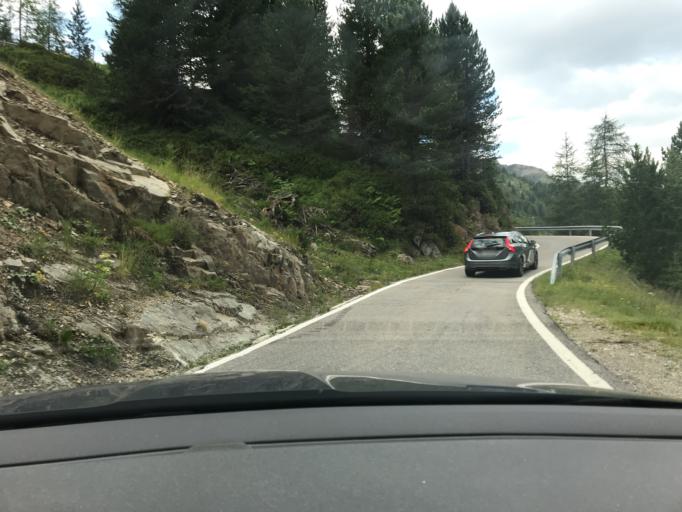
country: IT
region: Trentino-Alto Adige
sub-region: Bolzano
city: San Martino
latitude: 46.8891
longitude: 12.1972
